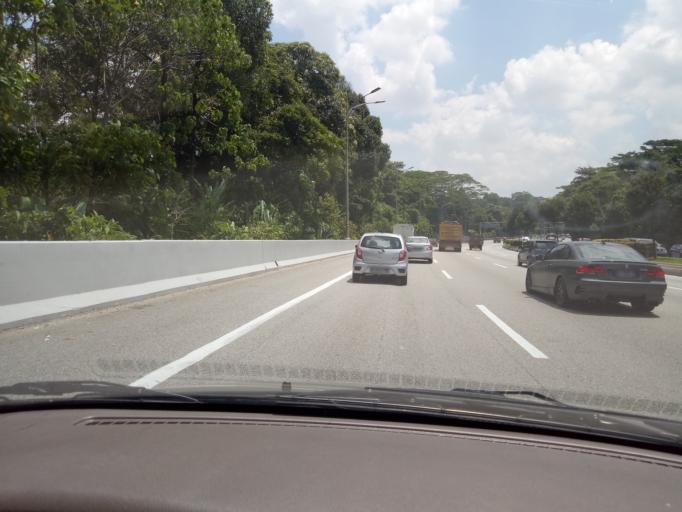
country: MY
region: Kuala Lumpur
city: Kuala Lumpur
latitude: 3.1245
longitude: 101.7029
